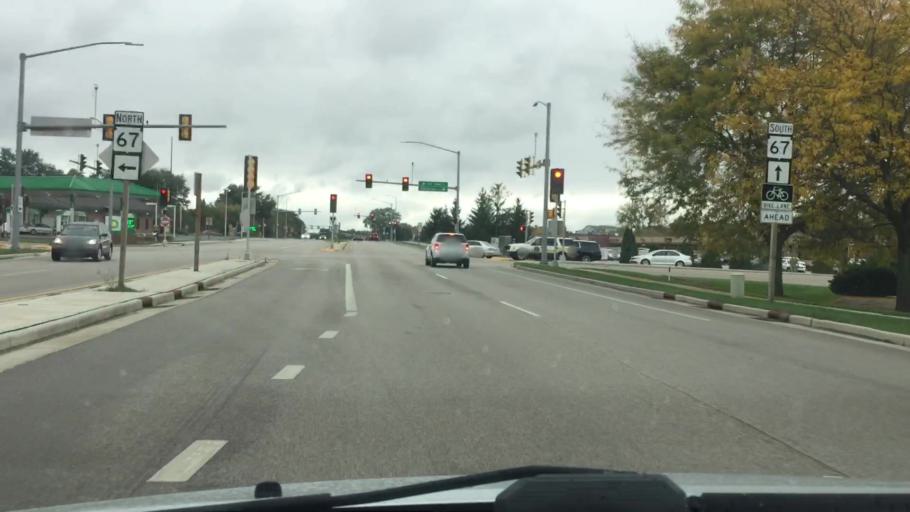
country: US
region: Wisconsin
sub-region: Waukesha County
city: Oconomowoc
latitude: 43.0974
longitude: -88.4820
